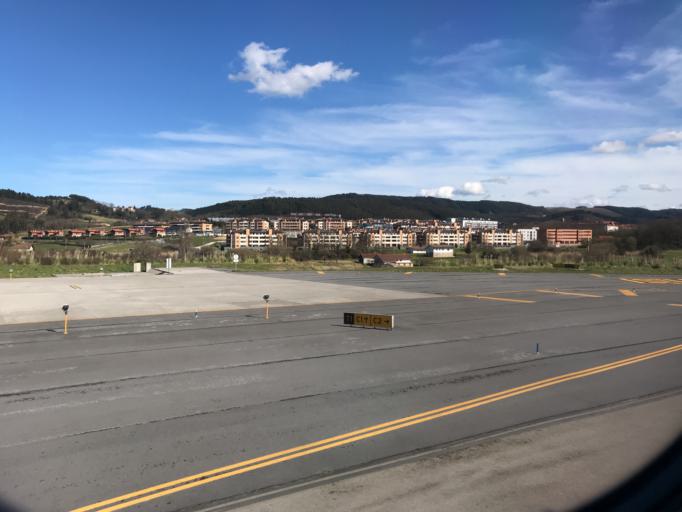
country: ES
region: Basque Country
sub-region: Bizkaia
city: Derio
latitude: 43.2979
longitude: -2.8968
